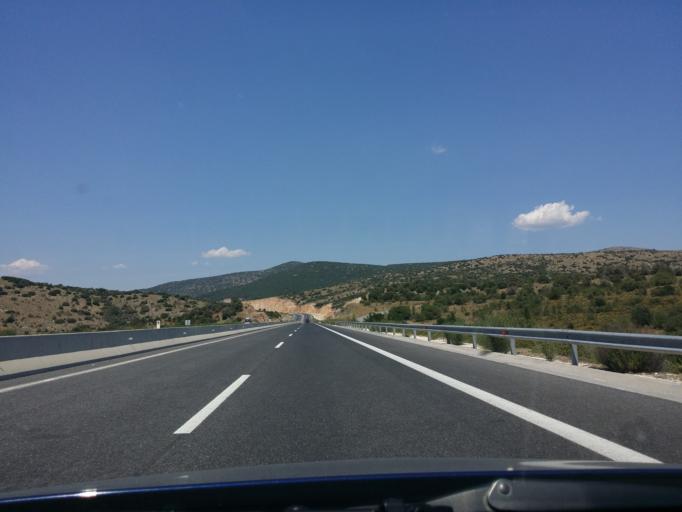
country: GR
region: Peloponnese
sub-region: Nomos Arkadias
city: Tripoli
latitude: 37.3943
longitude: 22.2925
